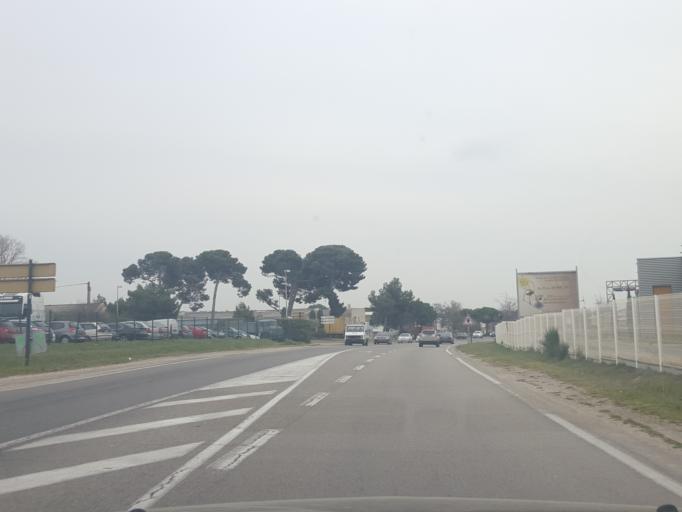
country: FR
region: Provence-Alpes-Cote d'Azur
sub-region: Departement du Vaucluse
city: Vedene
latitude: 43.9632
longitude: 4.8988
